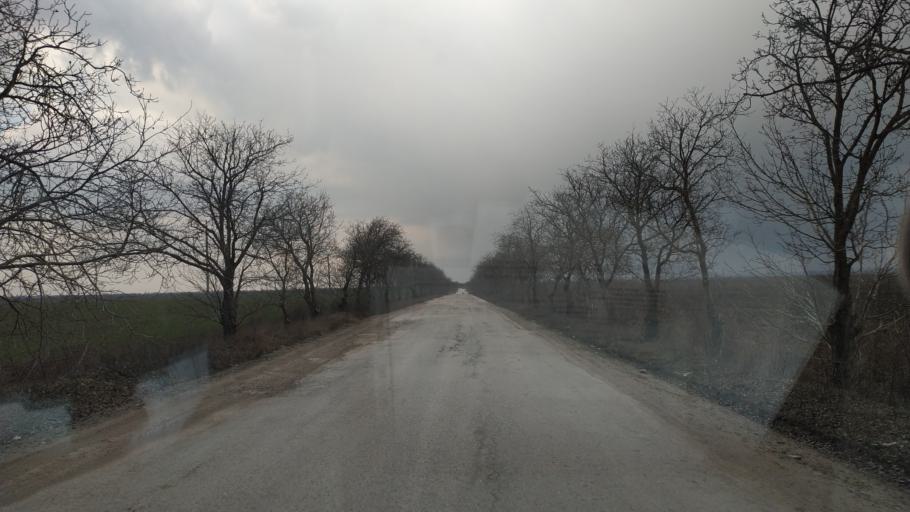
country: MD
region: Telenesti
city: Grigoriopol
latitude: 47.0335
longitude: 29.2926
